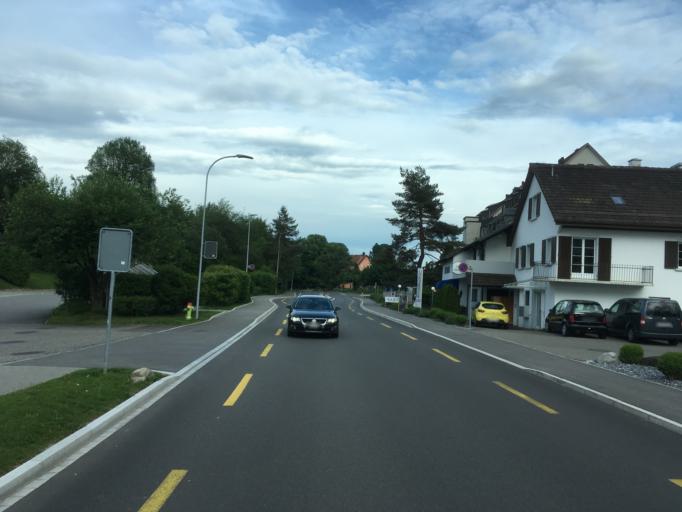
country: CH
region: Zurich
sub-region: Bezirk Uster
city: Ebmatingen
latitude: 47.3507
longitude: 8.6432
